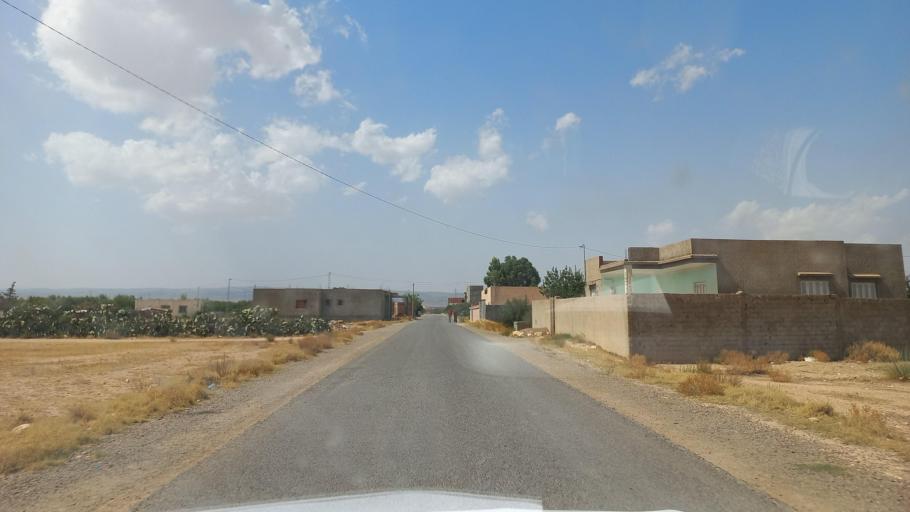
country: TN
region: Al Qasrayn
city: Kasserine
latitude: 35.2515
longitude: 9.0190
